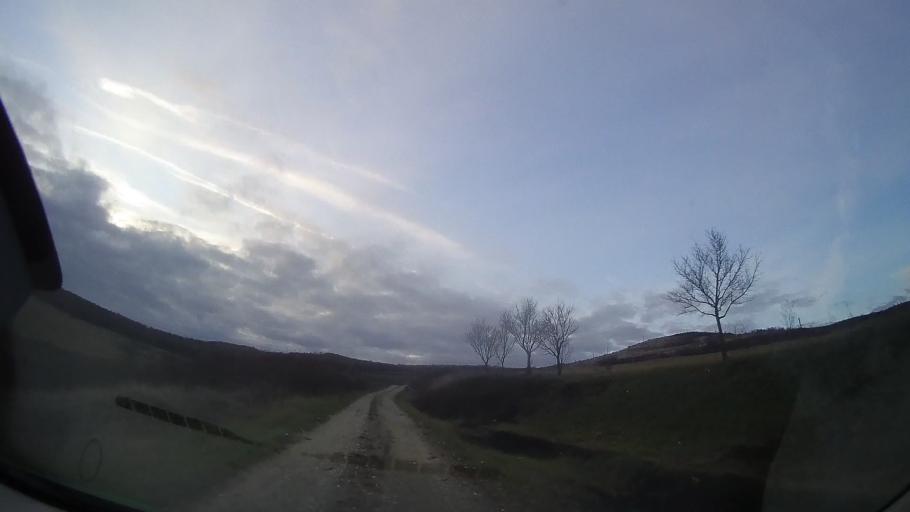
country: RO
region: Cluj
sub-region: Comuna Palatca
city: Palatca
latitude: 46.8571
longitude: 24.0362
